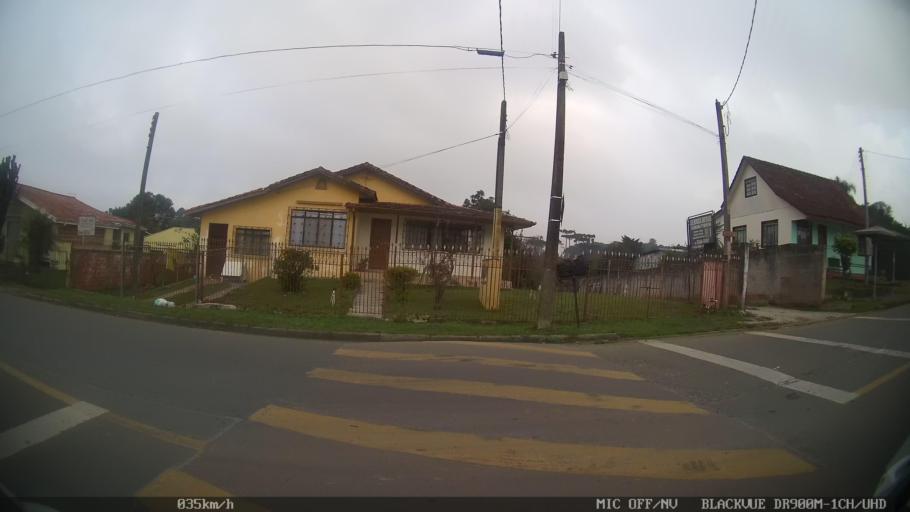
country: BR
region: Parana
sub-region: Almirante Tamandare
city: Almirante Tamandare
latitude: -25.3733
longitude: -49.3197
